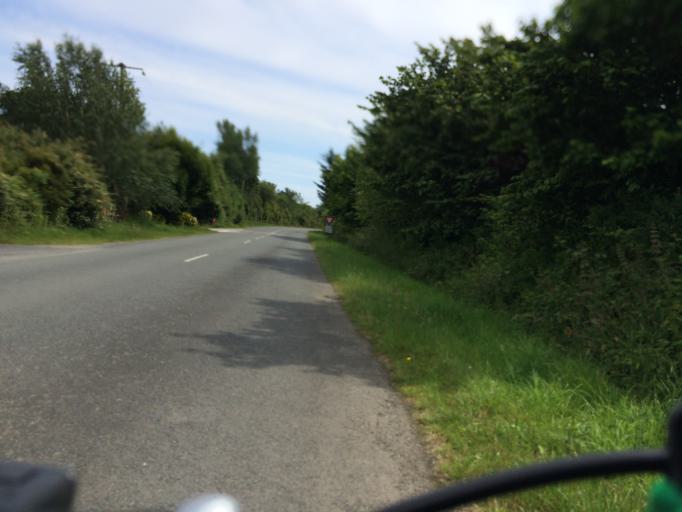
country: FR
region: Brittany
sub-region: Departement du Finistere
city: Logonna-Daoulas
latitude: 48.3209
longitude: -4.2962
